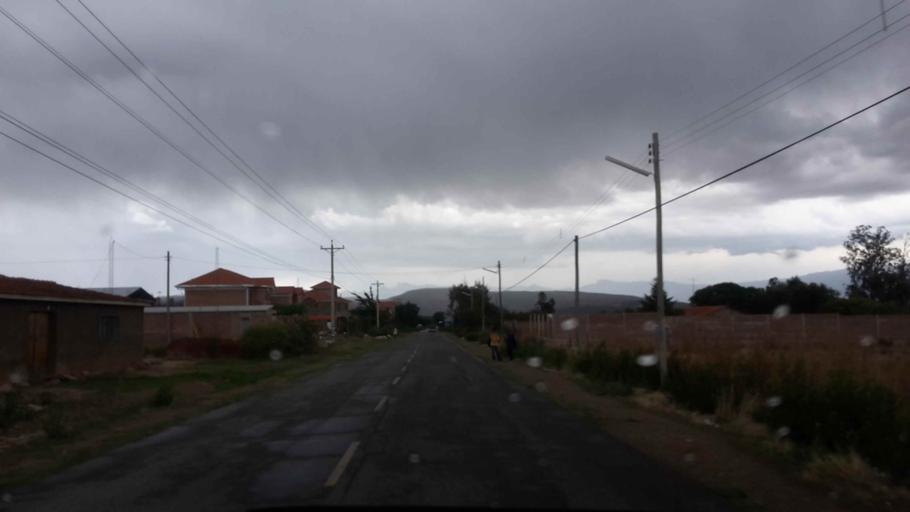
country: BO
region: Cochabamba
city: Tarata
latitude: -17.5800
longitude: -66.0570
